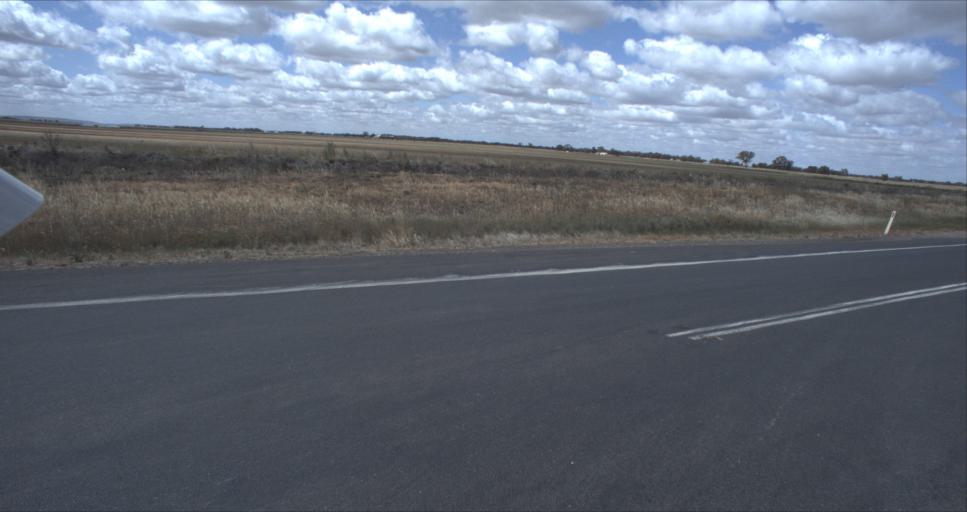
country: AU
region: New South Wales
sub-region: Murrumbidgee Shire
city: Darlington Point
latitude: -34.4973
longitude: 146.1888
